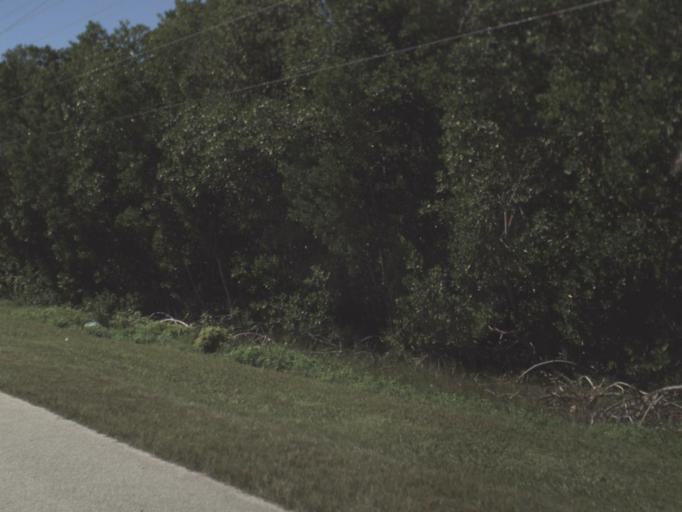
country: US
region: Florida
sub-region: Collier County
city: Marco
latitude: 25.9757
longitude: -81.7056
